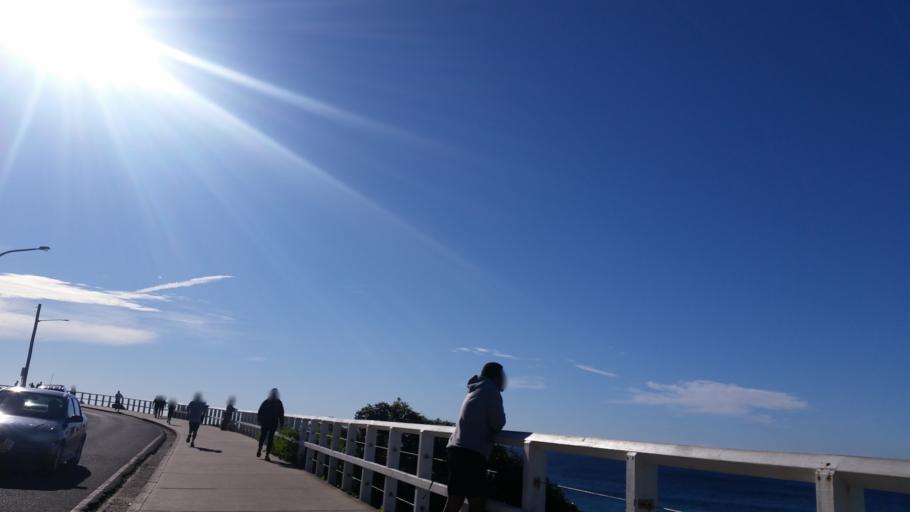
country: AU
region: New South Wales
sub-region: Waverley
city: Bronte
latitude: -33.9023
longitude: 151.2691
